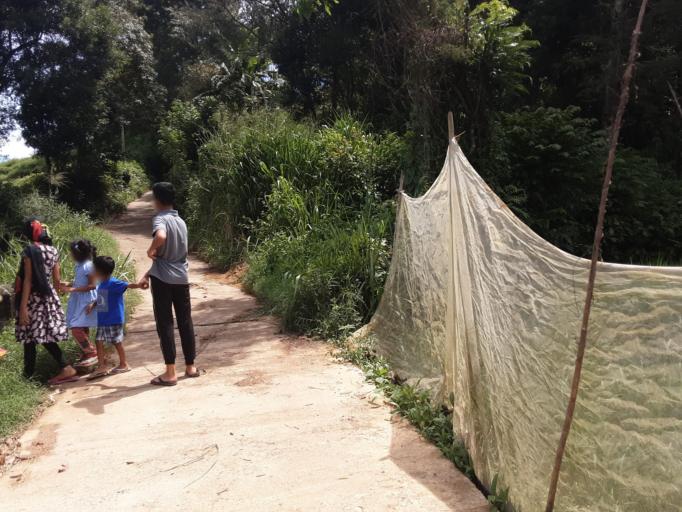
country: LK
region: Uva
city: Haputale
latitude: 6.8941
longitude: 80.9268
